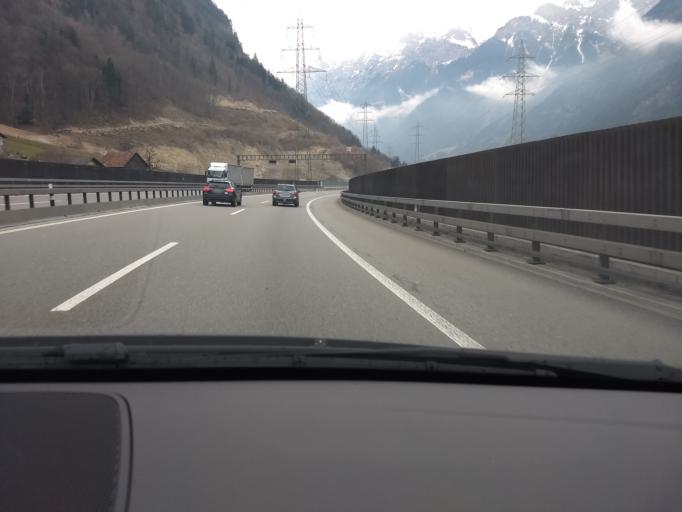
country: CH
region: Uri
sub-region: Uri
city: Silenen
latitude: 46.7757
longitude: 8.6655
